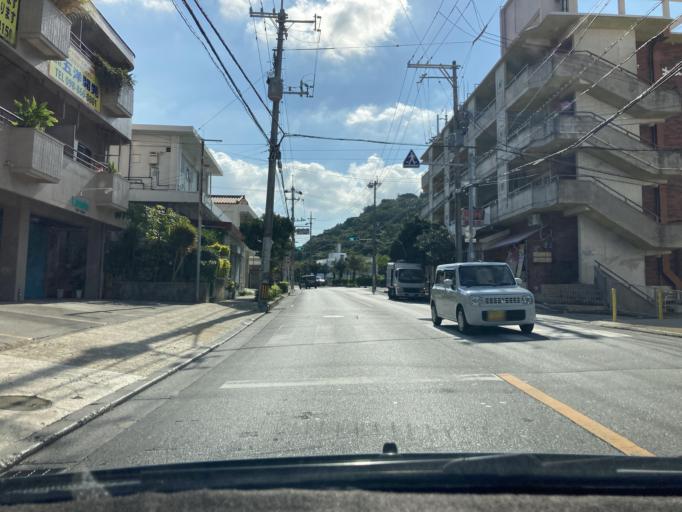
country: JP
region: Okinawa
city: Naha-shi
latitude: 26.2147
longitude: 127.7135
